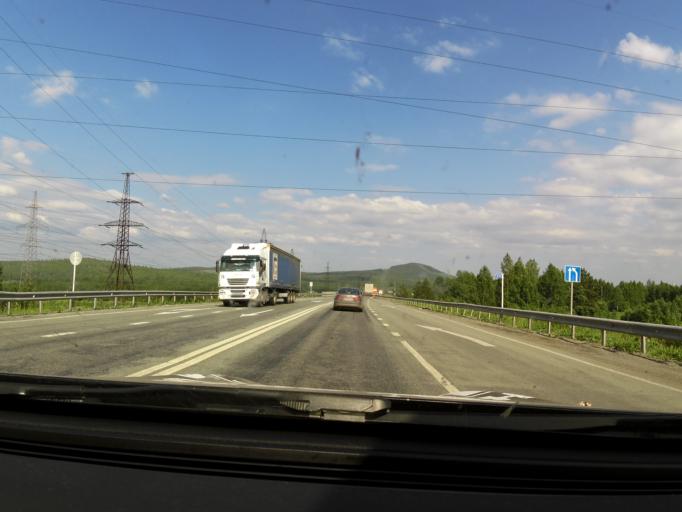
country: RU
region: Sverdlovsk
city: Revda
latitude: 56.8276
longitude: 59.9369
